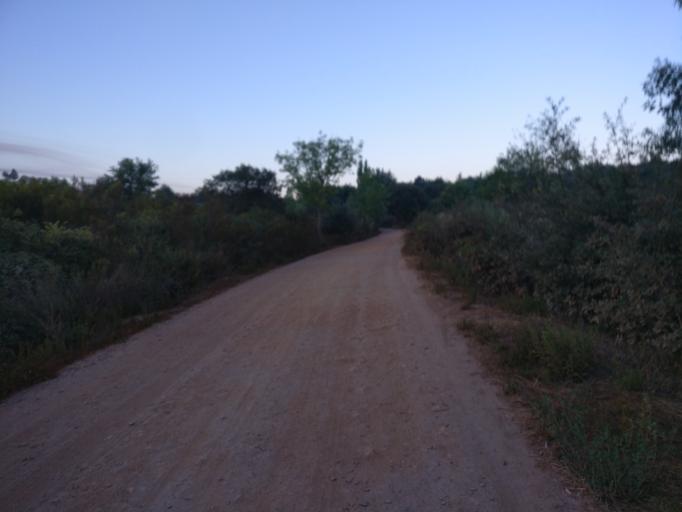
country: PT
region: Beja
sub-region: Odemira
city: Odemira
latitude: 37.7130
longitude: -8.5160
